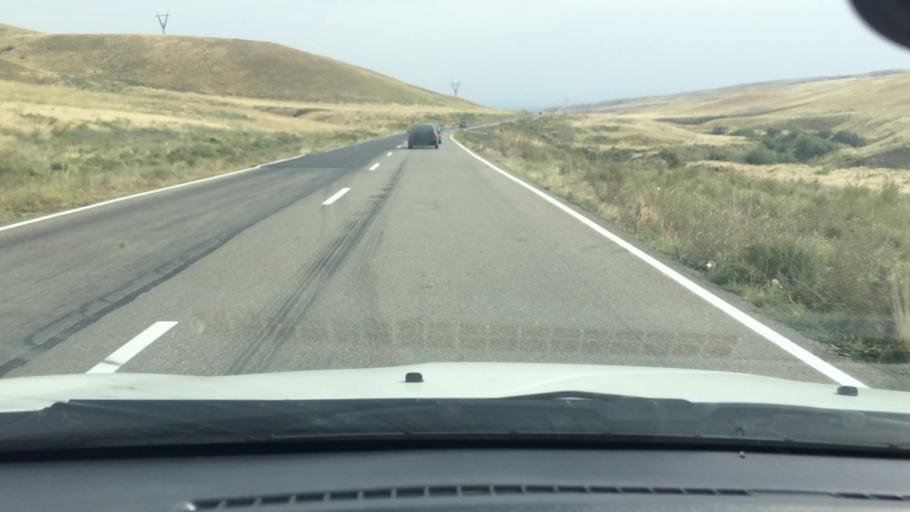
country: GE
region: Kvemo Kartli
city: Rust'avi
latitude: 41.5149
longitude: 44.9452
